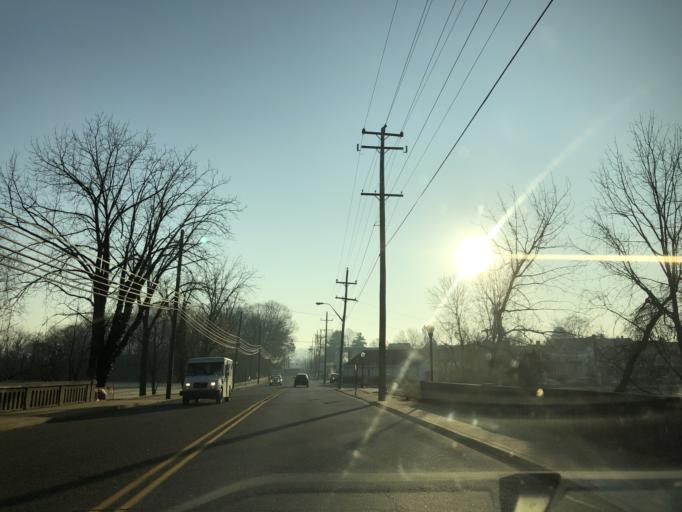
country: US
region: Pennsylvania
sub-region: Chester County
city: Downingtown
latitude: 40.0077
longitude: -75.7123
